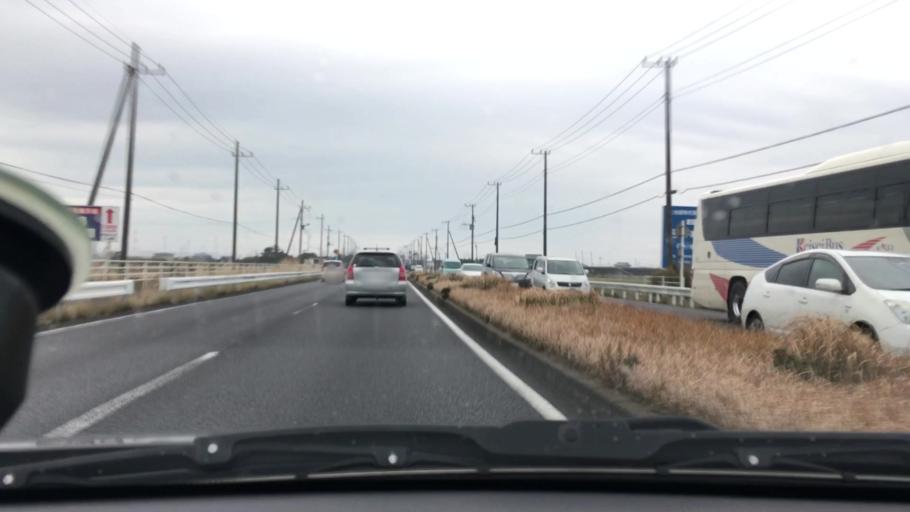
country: JP
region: Ibaraki
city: Kashima-shi
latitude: 35.9317
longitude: 140.6040
